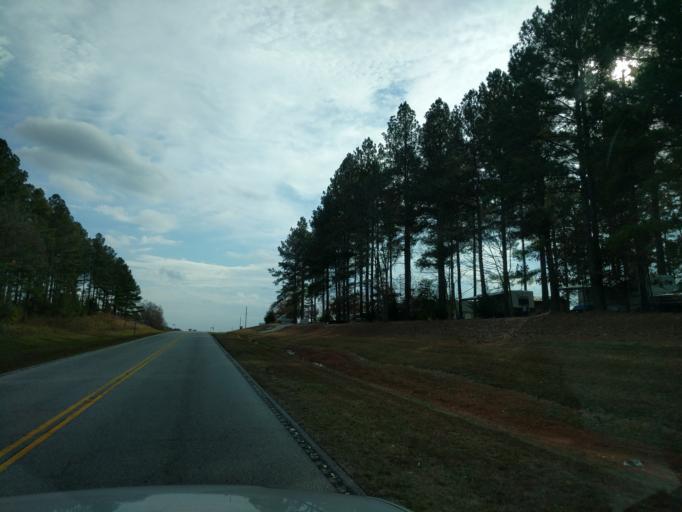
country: US
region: Georgia
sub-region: Franklin County
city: Gumlog
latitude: 34.5772
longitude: -83.0503
